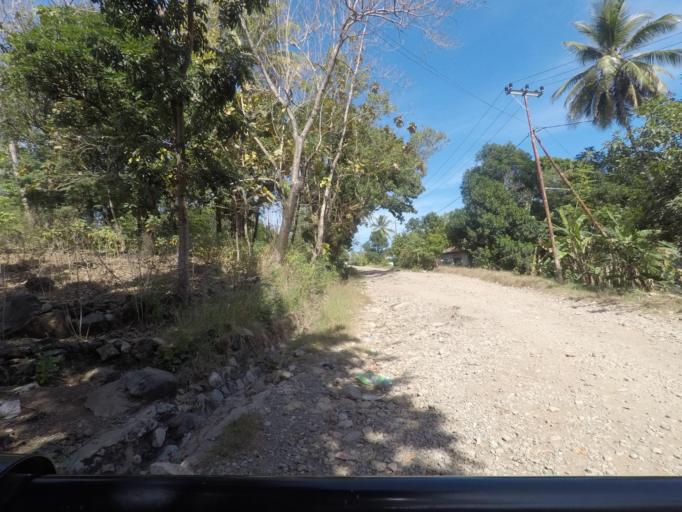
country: TL
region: Bobonaro
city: Maliana
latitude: -8.9929
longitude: 125.2193
